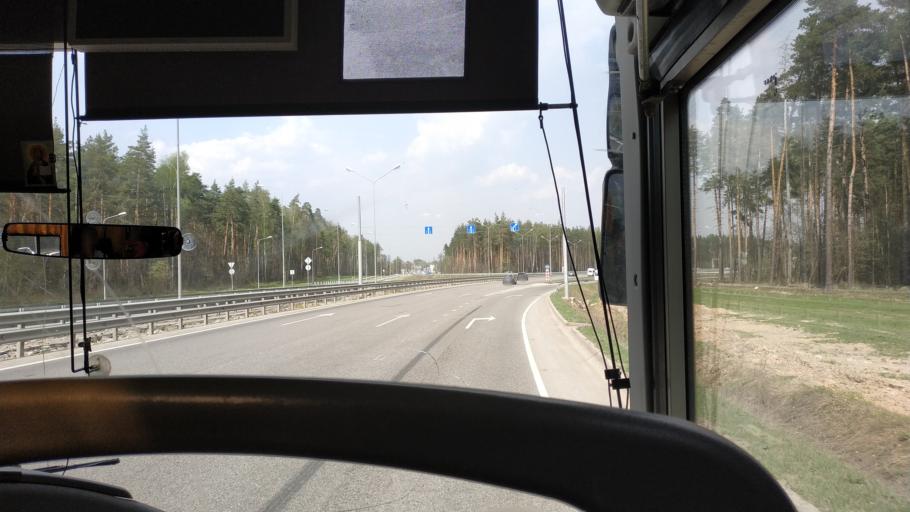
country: RU
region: Moskovskaya
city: Lytkarino
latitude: 55.6159
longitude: 37.9216
